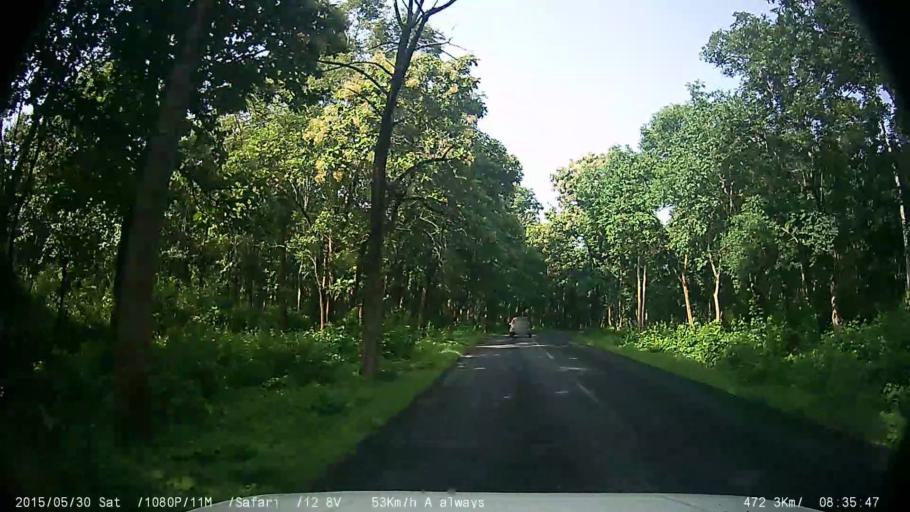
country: IN
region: Karnataka
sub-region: Mysore
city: Sargur
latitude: 11.7265
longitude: 76.4342
